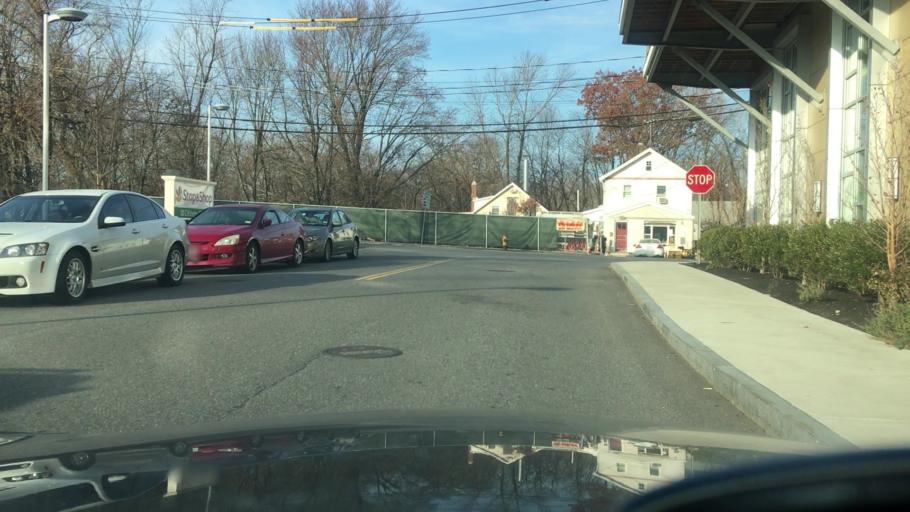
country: US
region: Massachusetts
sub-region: Middlesex County
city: Waltham
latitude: 42.3675
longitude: -71.2174
